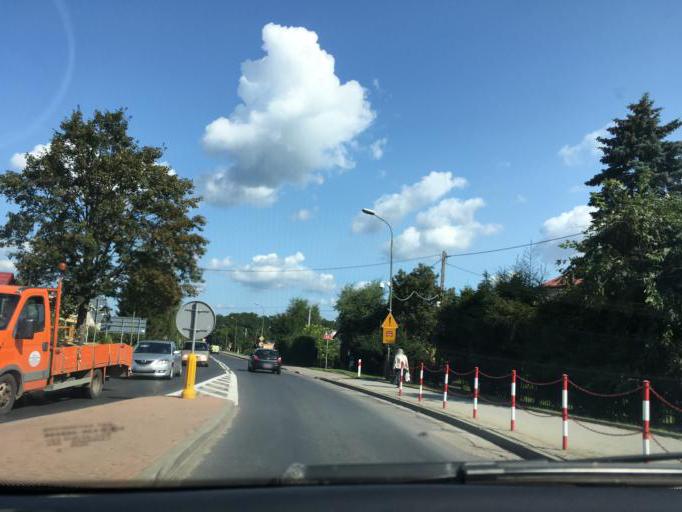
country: PL
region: Subcarpathian Voivodeship
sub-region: Powiat leski
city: Lesko
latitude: 49.4740
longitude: 22.3253
